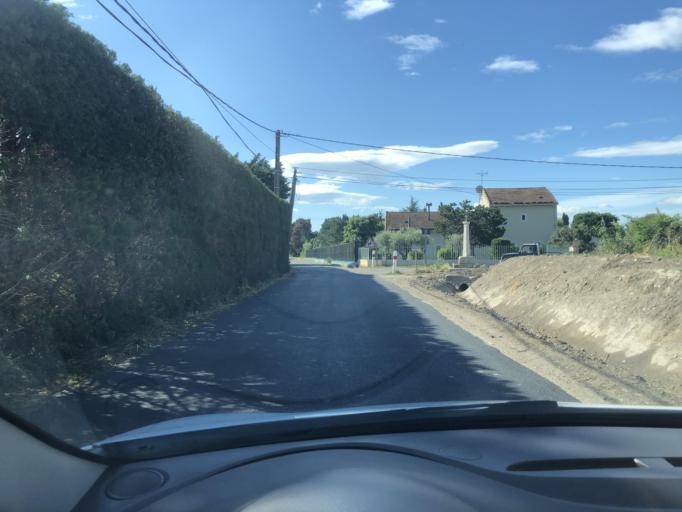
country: FR
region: Provence-Alpes-Cote d'Azur
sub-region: Departement des Bouches-du-Rhone
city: Rognonas
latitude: 43.9019
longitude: 4.8319
